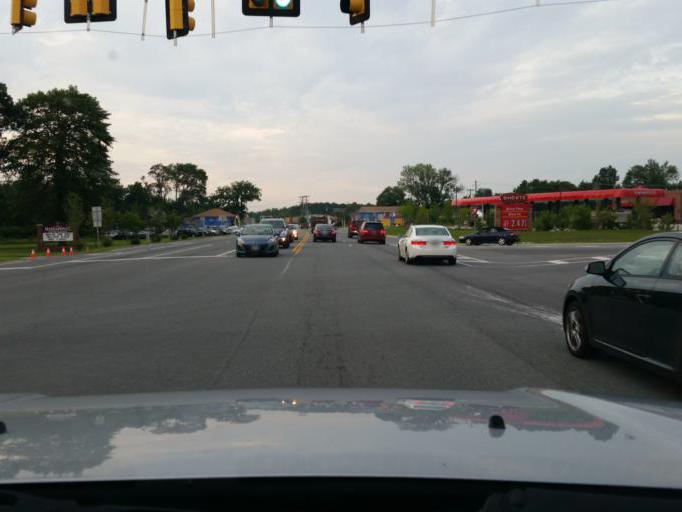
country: US
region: Virginia
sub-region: Spotsylvania County
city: Spotsylvania Courthouse
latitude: 38.1931
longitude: -77.5092
